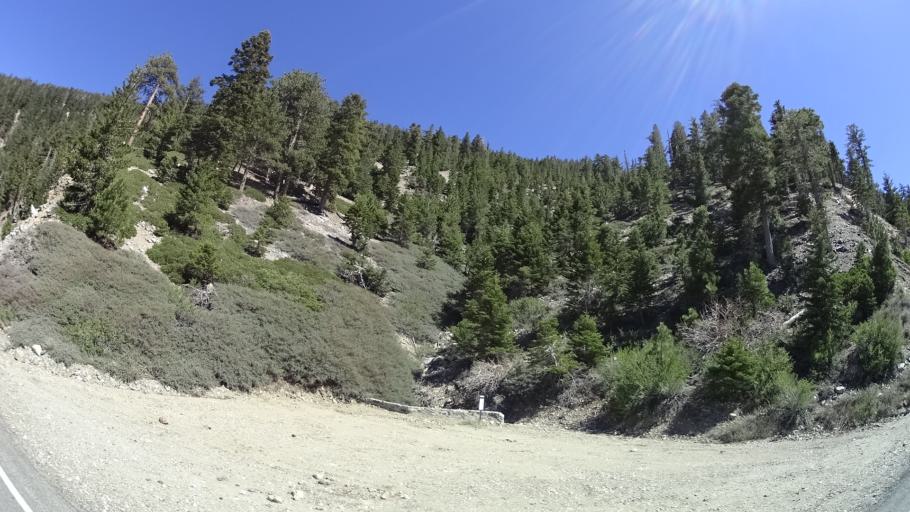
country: US
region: California
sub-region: San Bernardino County
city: Wrightwood
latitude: 34.3603
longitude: -117.7927
